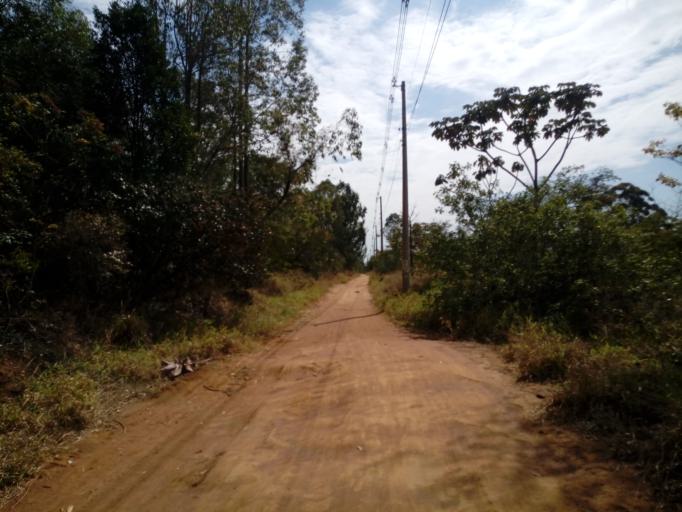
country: BR
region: Sao Paulo
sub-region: Sao Carlos
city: Sao Carlos
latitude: -21.9773
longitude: -47.8757
